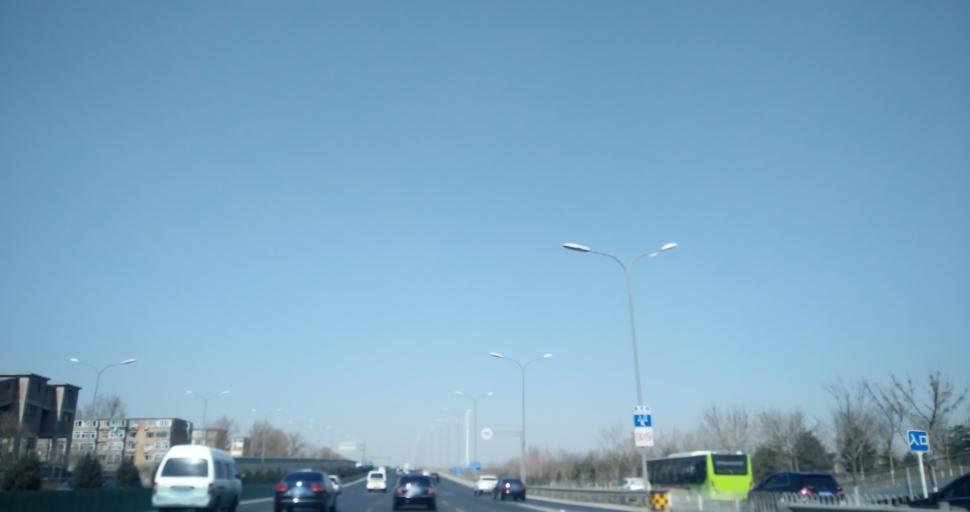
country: CN
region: Beijing
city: Jiugong
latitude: 39.7941
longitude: 116.4238
